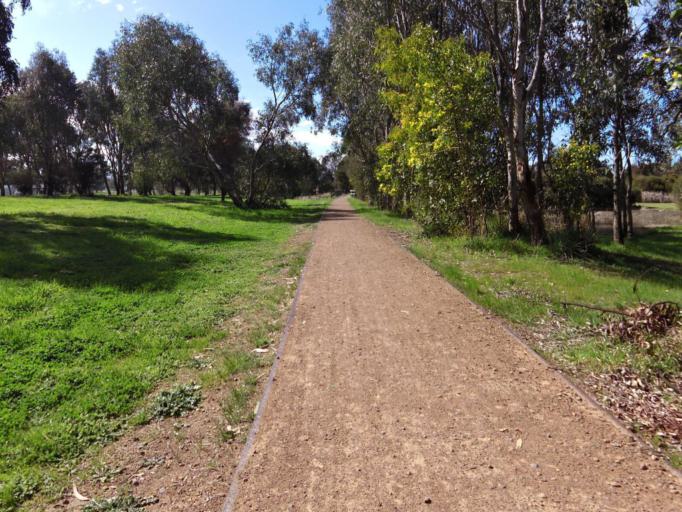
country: AU
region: Victoria
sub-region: Mansfield
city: Mansfield
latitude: -37.0496
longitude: 146.0744
